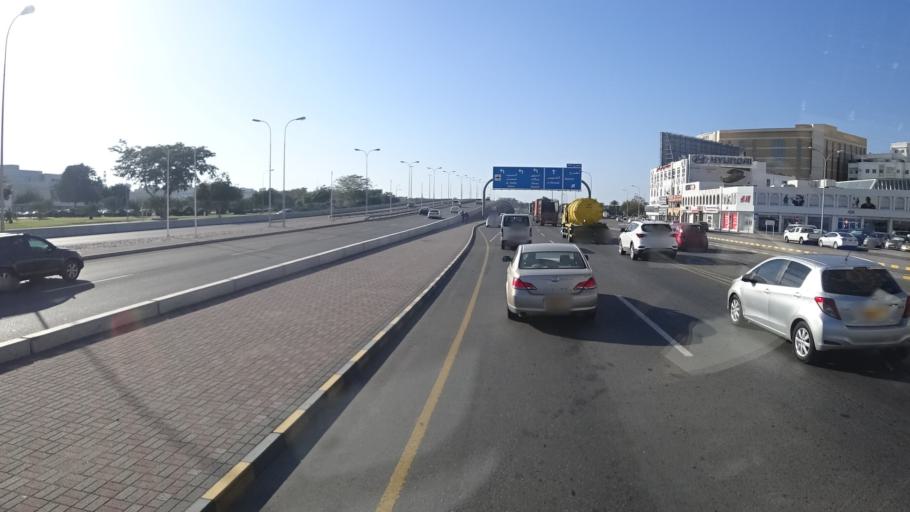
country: OM
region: Muhafazat Masqat
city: Muscat
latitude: 23.6106
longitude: 58.4957
